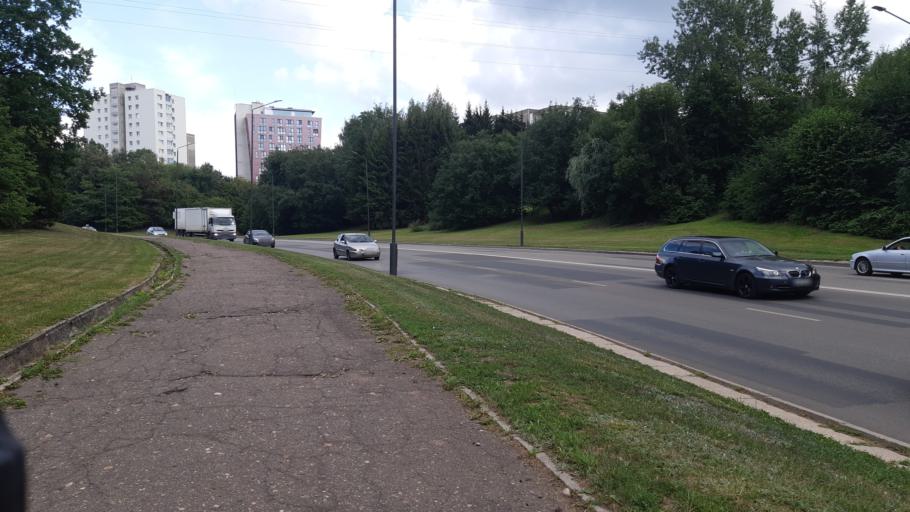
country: LT
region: Kauno apskritis
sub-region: Kaunas
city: Eiguliai
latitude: 54.9278
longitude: 23.9212
